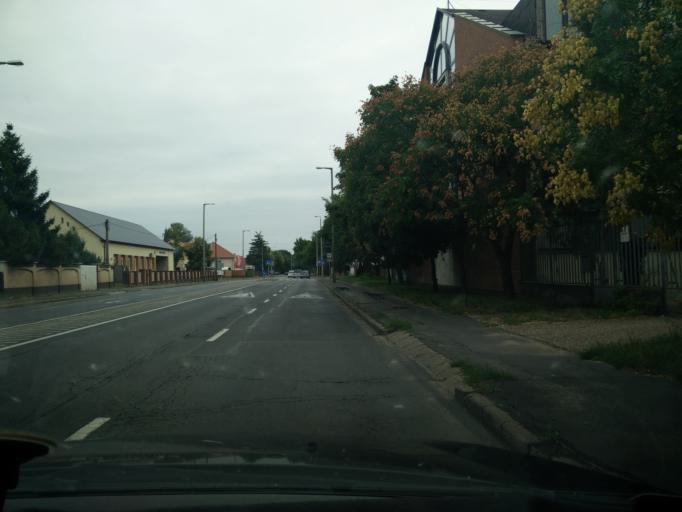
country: HU
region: Hajdu-Bihar
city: Debrecen
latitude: 47.5289
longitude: 21.6552
